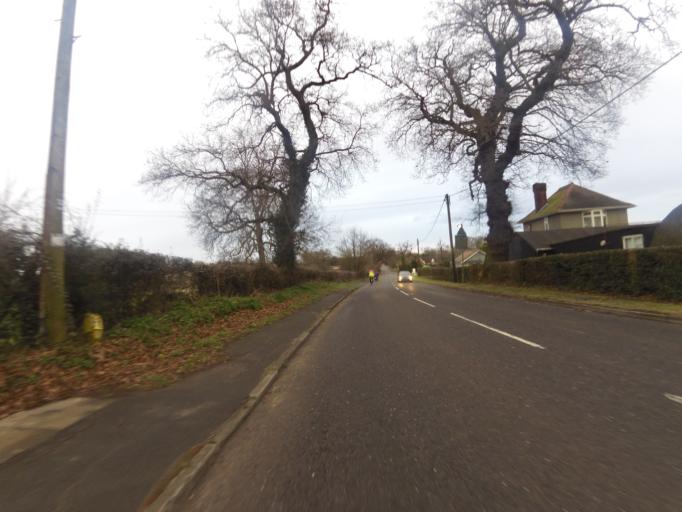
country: GB
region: England
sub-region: Suffolk
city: Ipswich
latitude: 52.0821
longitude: 1.1669
